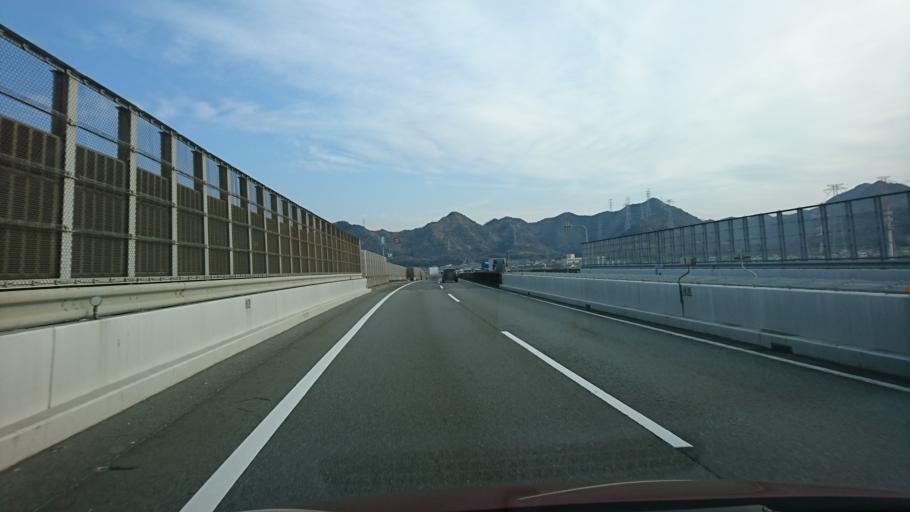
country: JP
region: Hyogo
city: Shirahamacho-usazakiminami
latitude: 34.8109
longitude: 134.7444
